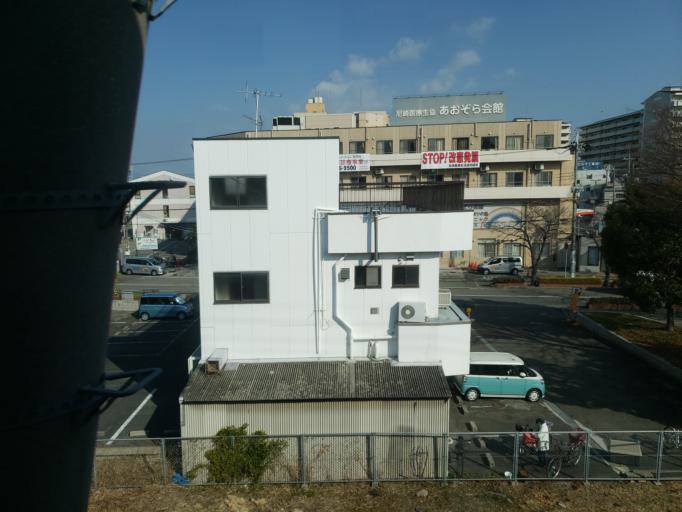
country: JP
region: Hyogo
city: Amagasaki
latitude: 34.7392
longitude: 135.3860
